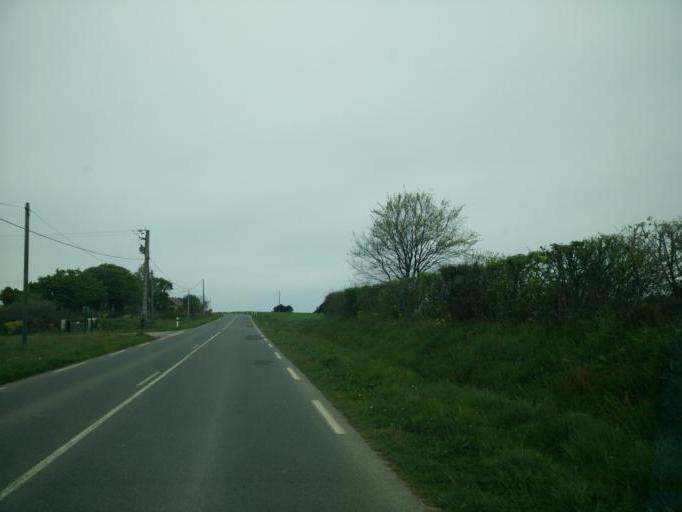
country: FR
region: Brittany
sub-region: Departement des Cotes-d'Armor
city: Langoat
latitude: 48.7656
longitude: -3.3057
